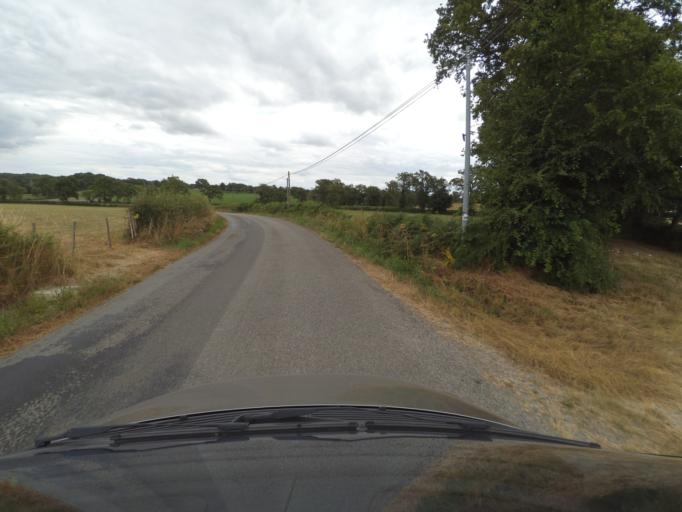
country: FR
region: Limousin
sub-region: Departement de la Haute-Vienne
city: Magnac-Laval
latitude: 46.2835
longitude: 1.2525
